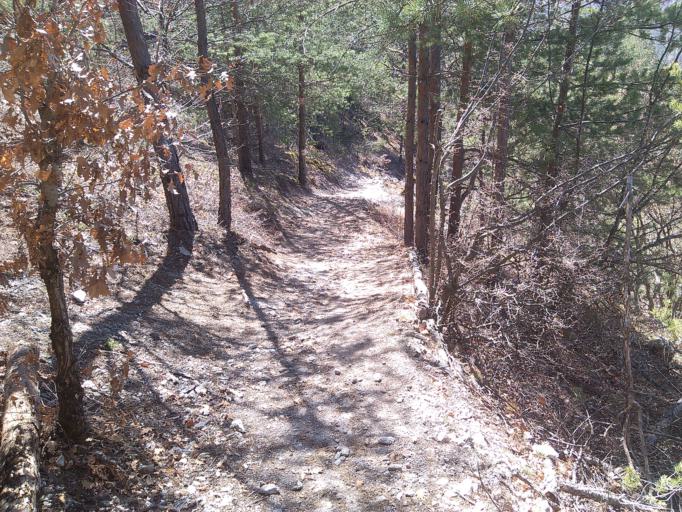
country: BG
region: Kurdzhali
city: Ardino
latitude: 41.5668
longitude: 25.1472
